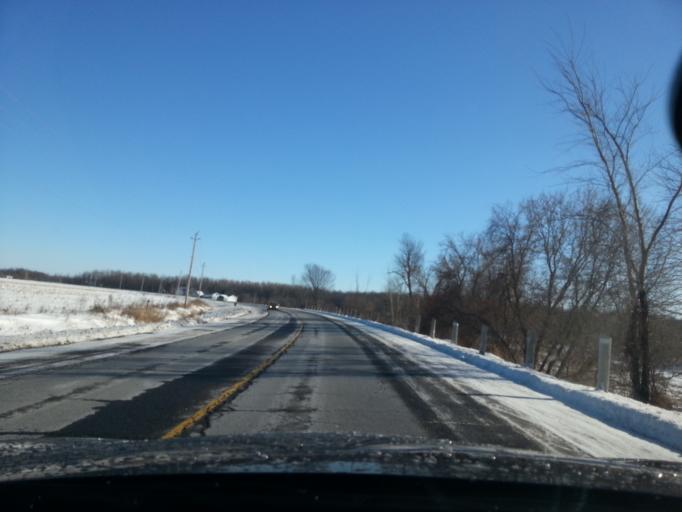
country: CA
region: Ontario
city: Bourget
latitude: 45.2543
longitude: -75.3903
